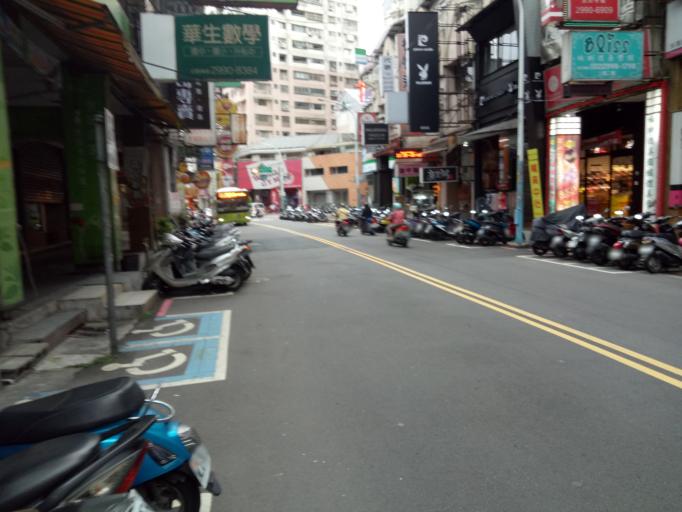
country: TW
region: Taipei
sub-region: Taipei
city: Banqiao
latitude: 25.0503
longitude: 121.4476
